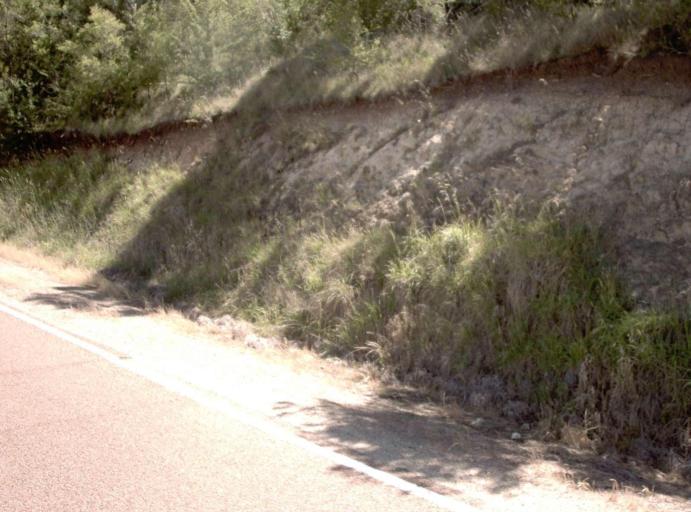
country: AU
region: Victoria
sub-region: East Gippsland
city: Lakes Entrance
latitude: -37.4786
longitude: 148.1814
